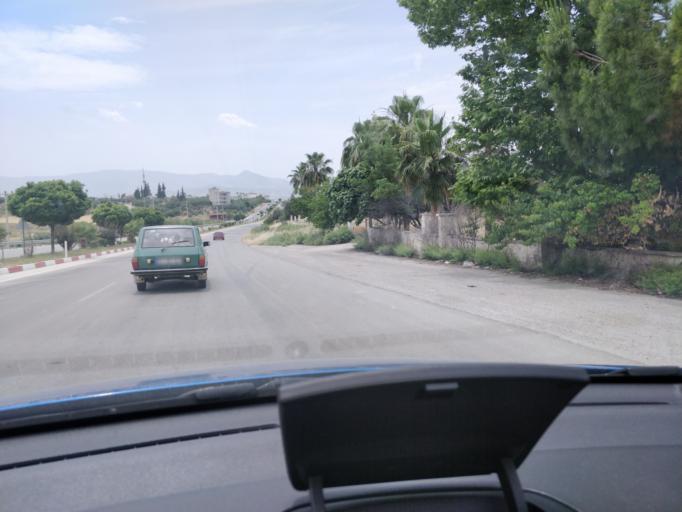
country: TR
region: Mersin
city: Mut
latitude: 36.6149
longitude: 33.4411
